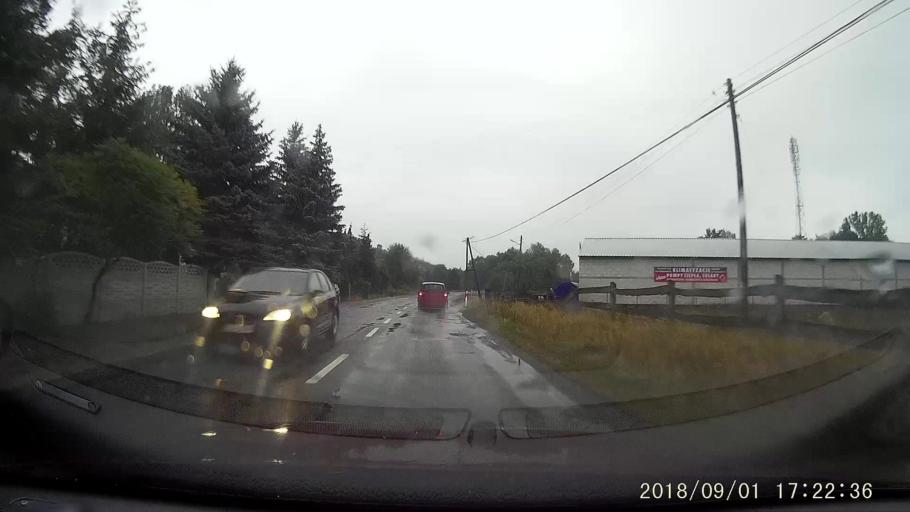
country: PL
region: Lubusz
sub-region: Powiat zaganski
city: Zagan
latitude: 51.7049
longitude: 15.2922
